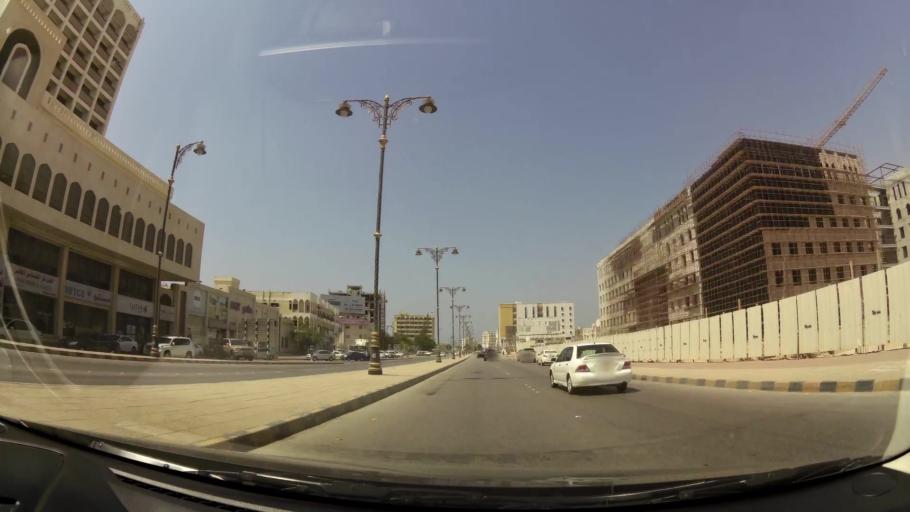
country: OM
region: Zufar
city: Salalah
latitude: 17.0241
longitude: 54.1114
